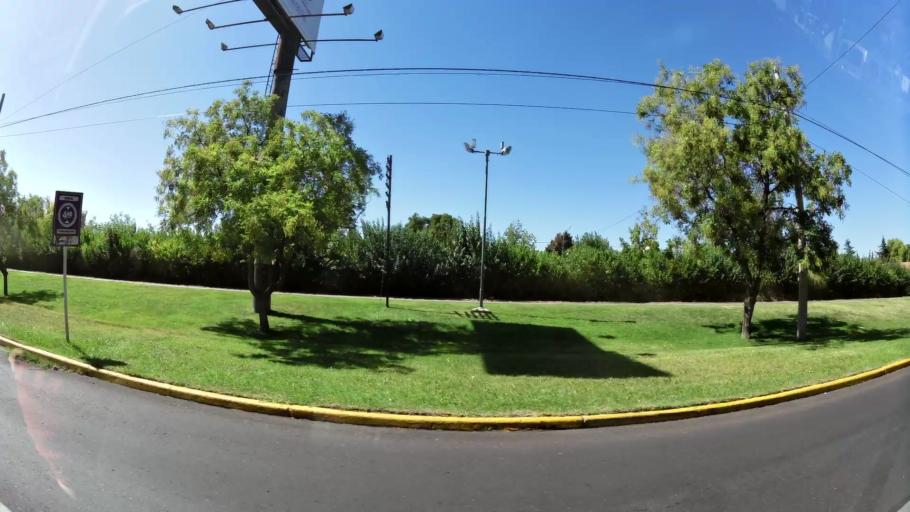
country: AR
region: Mendoza
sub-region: Departamento de Godoy Cruz
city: Godoy Cruz
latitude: -32.9482
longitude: -68.8534
